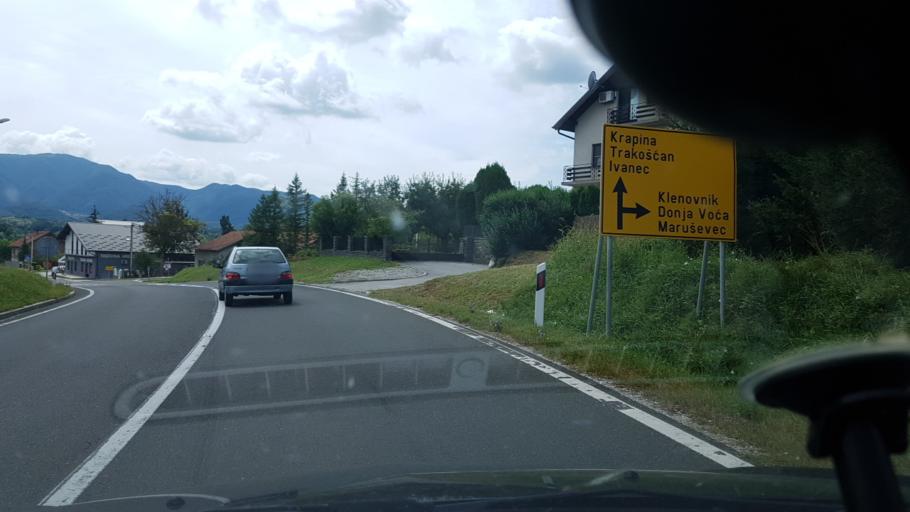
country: HR
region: Varazdinska
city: Ivanec
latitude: 46.2451
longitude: 16.1754
